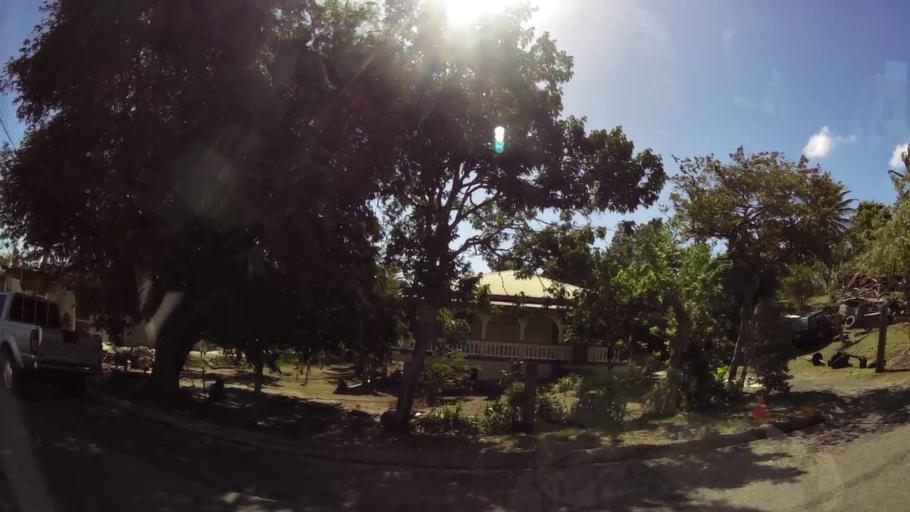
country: LC
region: Laborie Quarter
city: Laborie
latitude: 13.7507
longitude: -60.9689
